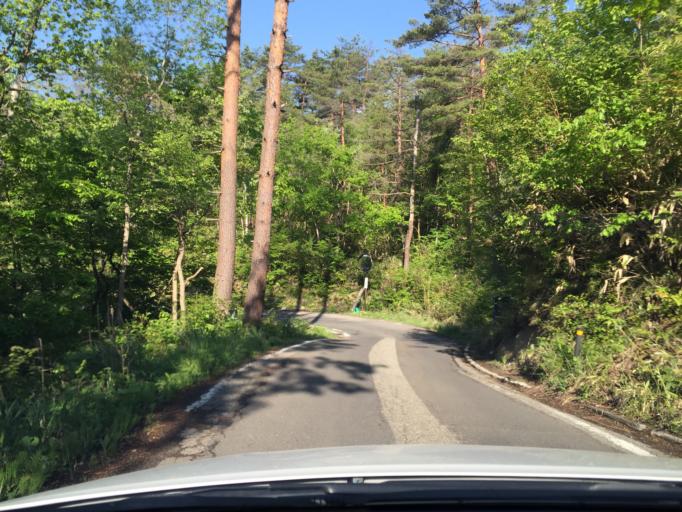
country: JP
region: Fukushima
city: Kitakata
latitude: 37.6697
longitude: 139.8311
